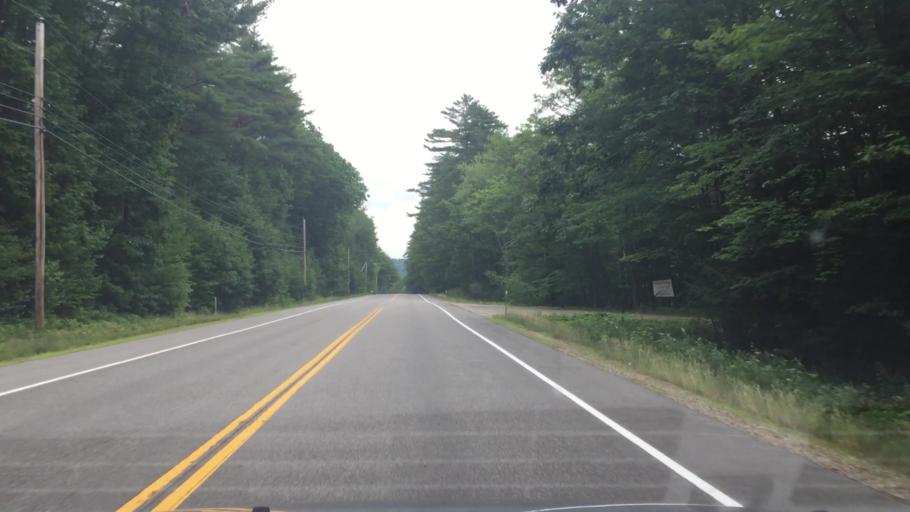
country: US
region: New Hampshire
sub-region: Carroll County
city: Sandwich
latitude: 43.8201
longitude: -71.3488
